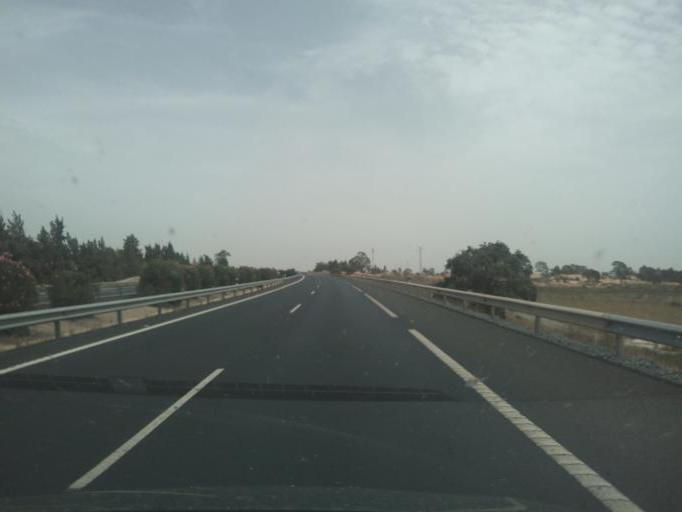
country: ES
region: Andalusia
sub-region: Provincia de Huelva
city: Villarrasa
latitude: 37.3451
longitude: -6.6261
